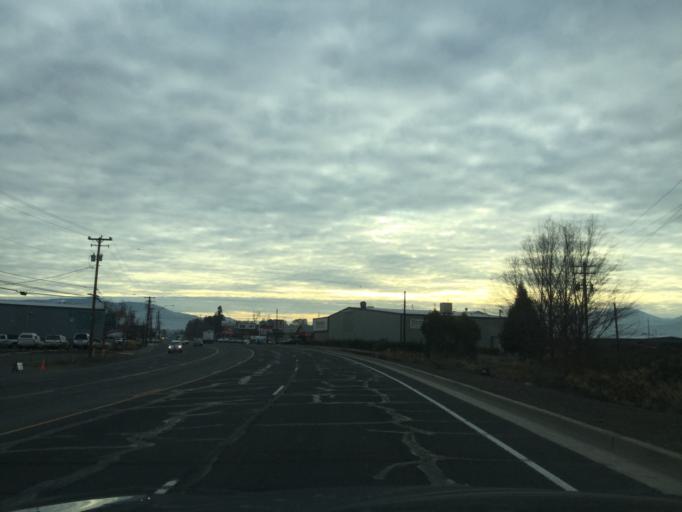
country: US
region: Oregon
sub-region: Jackson County
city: Central Point
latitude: 42.3519
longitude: -122.8978
